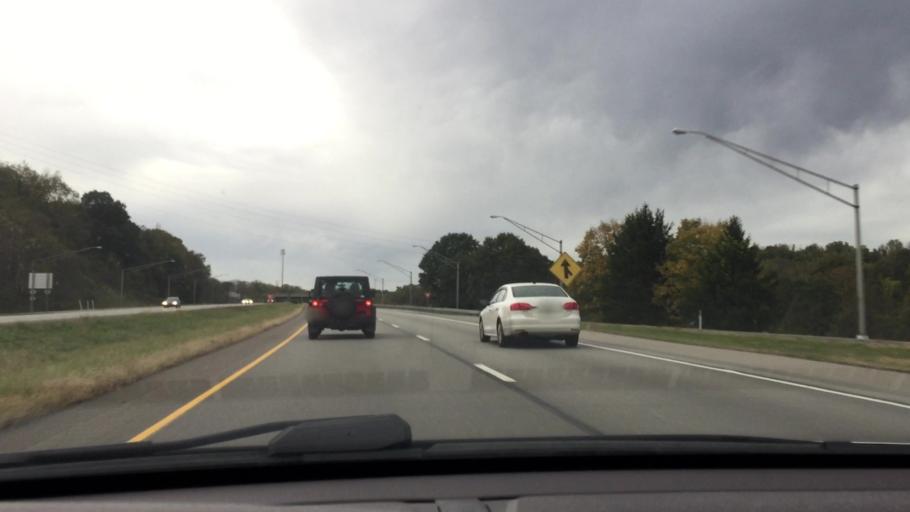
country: US
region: Pennsylvania
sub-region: Beaver County
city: Beaver
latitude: 40.7036
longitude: -80.3666
